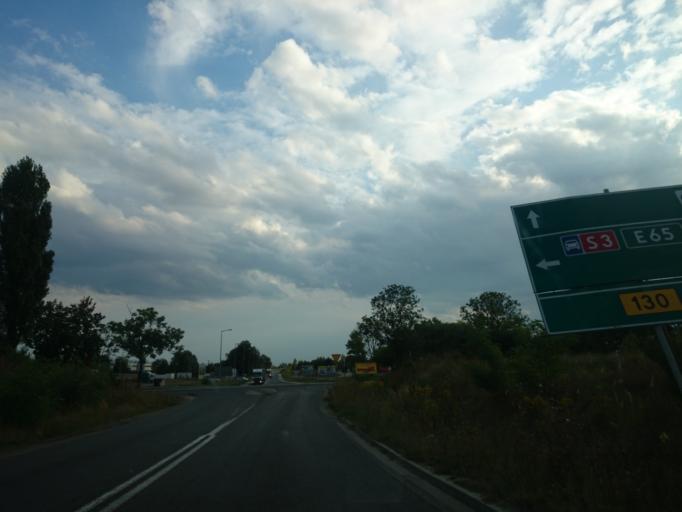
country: PL
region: Lubusz
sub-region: Powiat gorzowski
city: Klodawa
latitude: 52.7463
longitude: 15.1566
